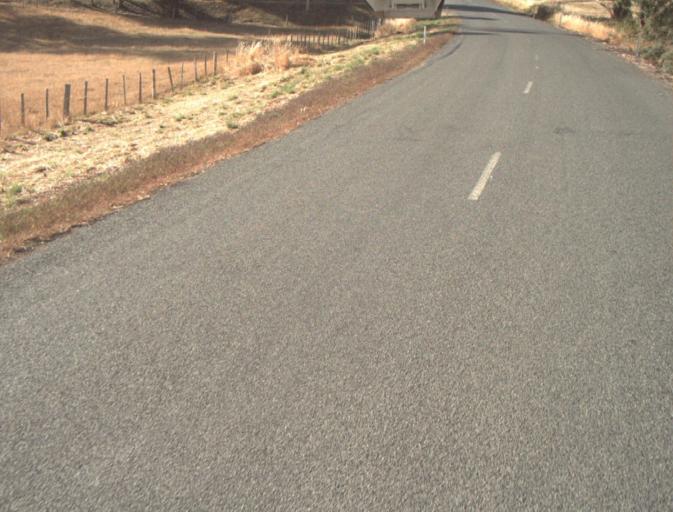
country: AU
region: Tasmania
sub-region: Launceston
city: Mayfield
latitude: -41.2002
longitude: 147.2174
